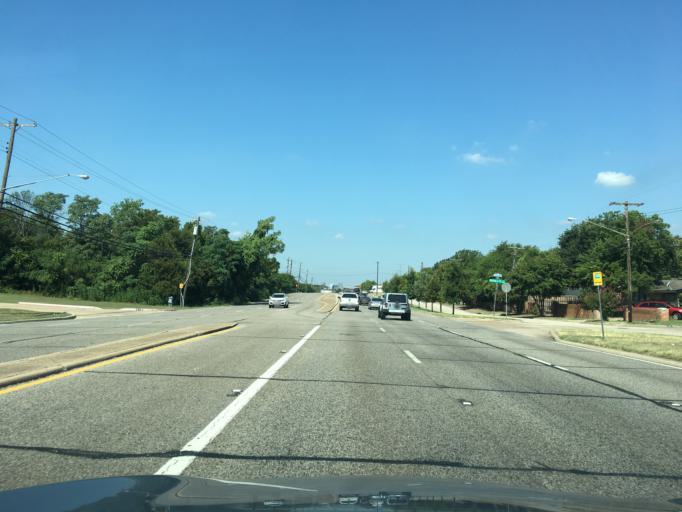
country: US
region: Texas
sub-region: Dallas County
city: Garland
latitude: 32.8643
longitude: -96.6925
